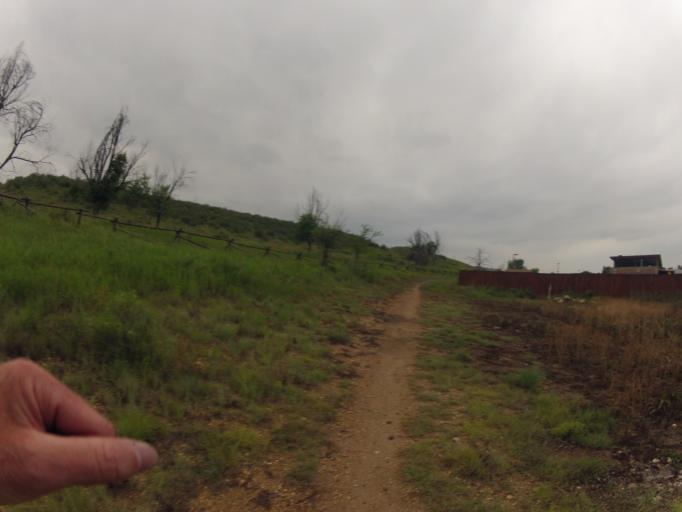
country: US
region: Colorado
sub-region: Larimer County
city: Fort Collins
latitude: 40.5411
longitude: -105.1297
